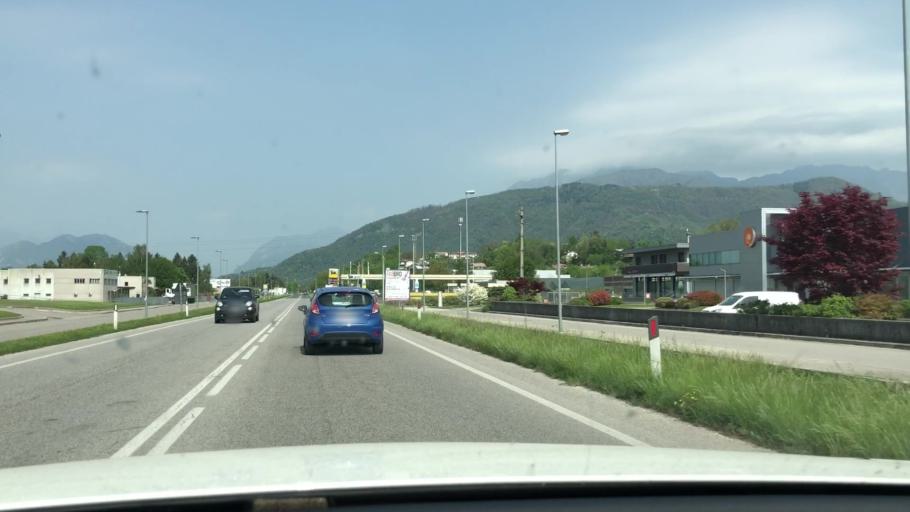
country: IT
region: Friuli Venezia Giulia
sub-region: Provincia di Udine
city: Magnano in Riviera
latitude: 46.2047
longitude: 13.1890
